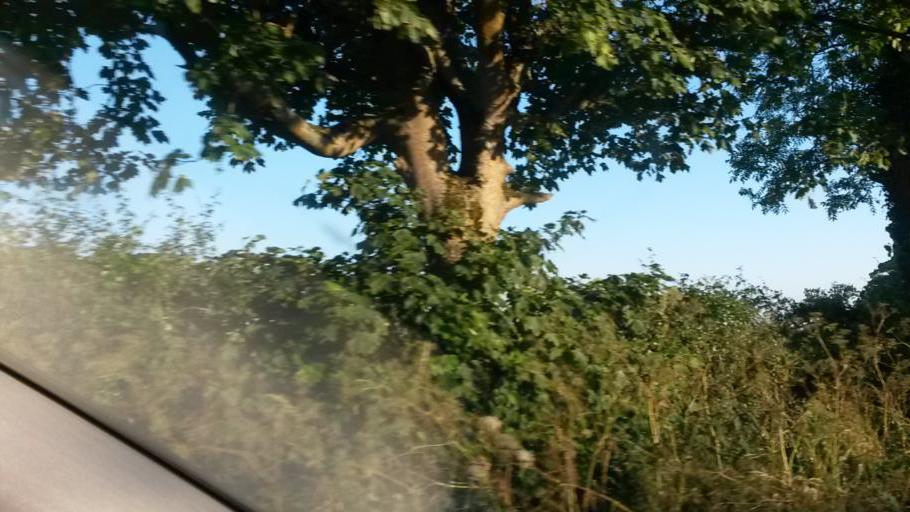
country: IE
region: Leinster
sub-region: An Mhi
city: Ashbourne
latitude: 53.5449
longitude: -6.3608
